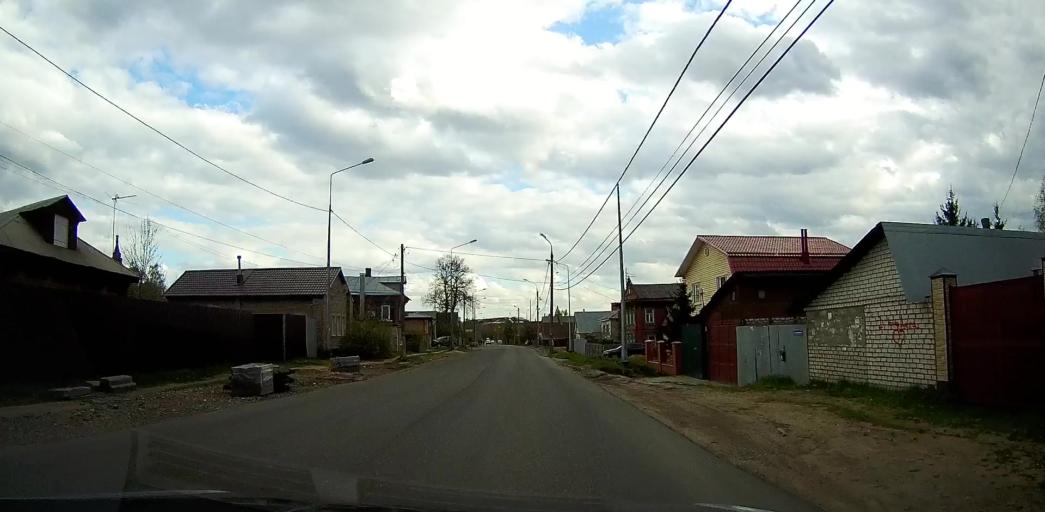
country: RU
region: Moskovskaya
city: Pavlovskiy Posad
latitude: 55.7895
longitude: 38.6852
